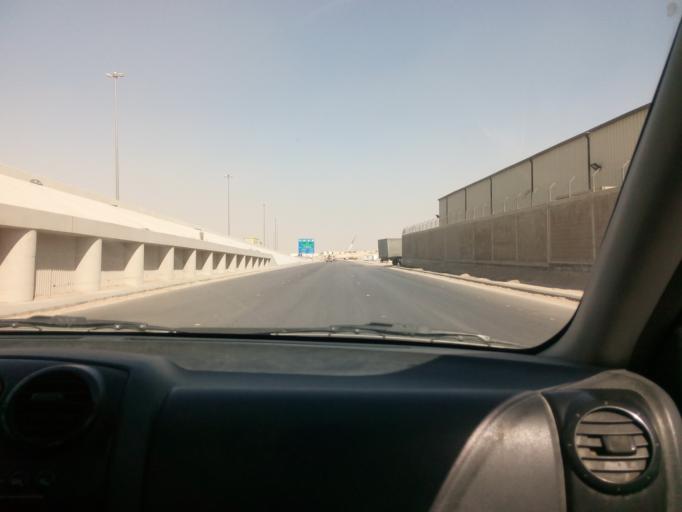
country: SA
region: Ar Riyad
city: Riyadh
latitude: 24.6468
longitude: 46.8432
